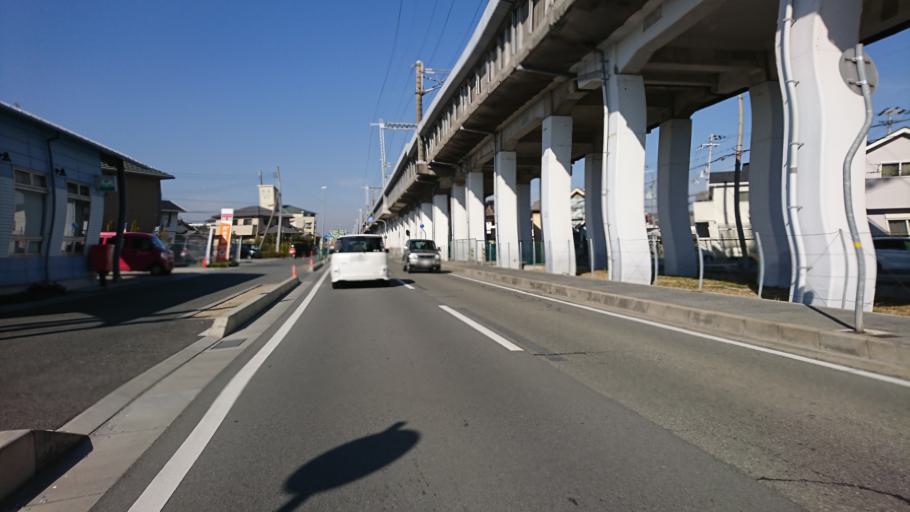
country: JP
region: Hyogo
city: Kakogawacho-honmachi
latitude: 34.7687
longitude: 134.7965
